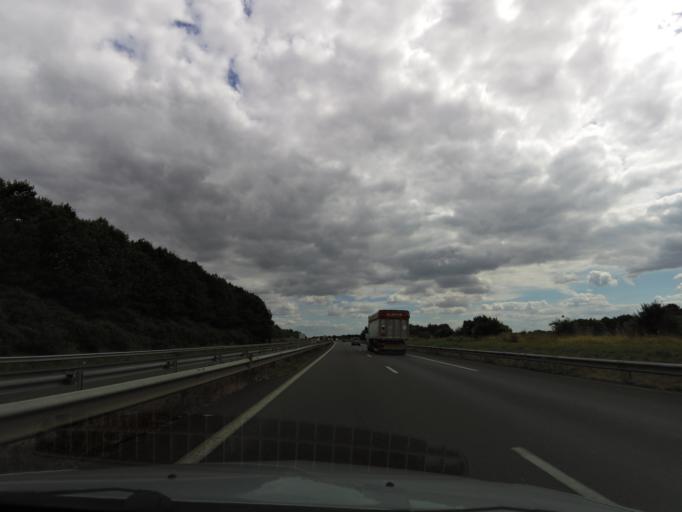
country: FR
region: Pays de la Loire
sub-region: Departement de la Loire-Atlantique
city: Le Bignon
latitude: 47.1102
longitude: -1.4878
